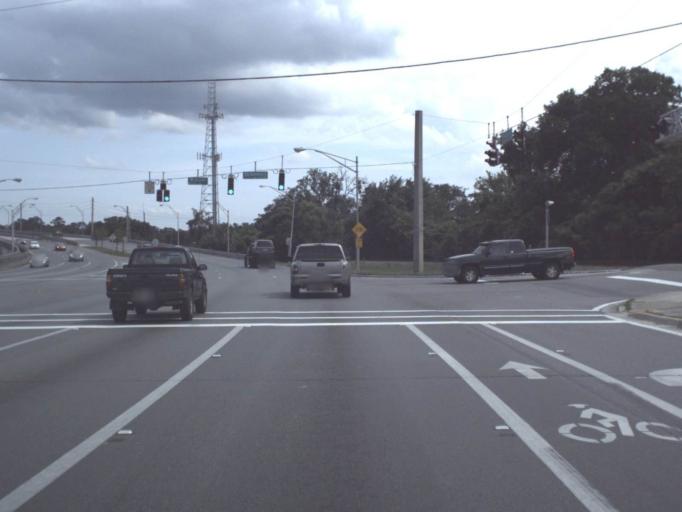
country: US
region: Florida
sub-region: Duval County
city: Jacksonville
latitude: 30.2778
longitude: -81.7202
